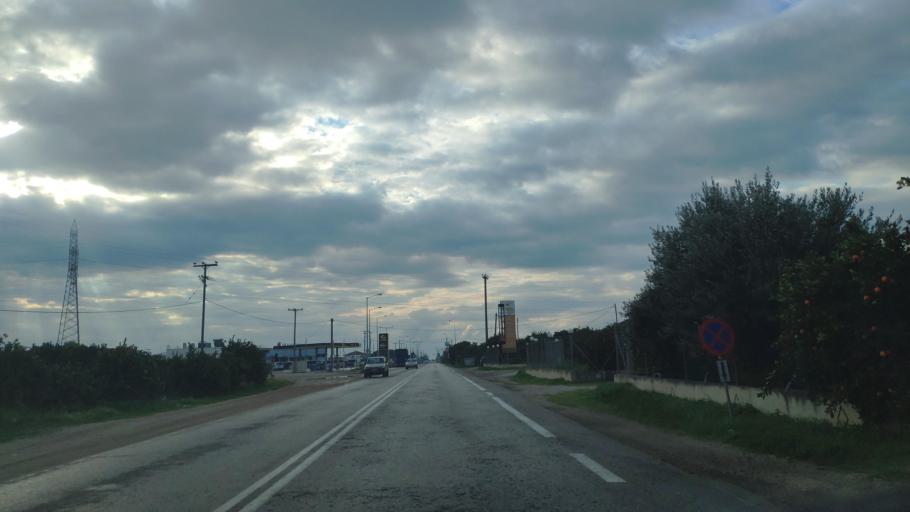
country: GR
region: Peloponnese
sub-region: Nomos Argolidos
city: Argos
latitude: 37.6585
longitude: 22.7261
